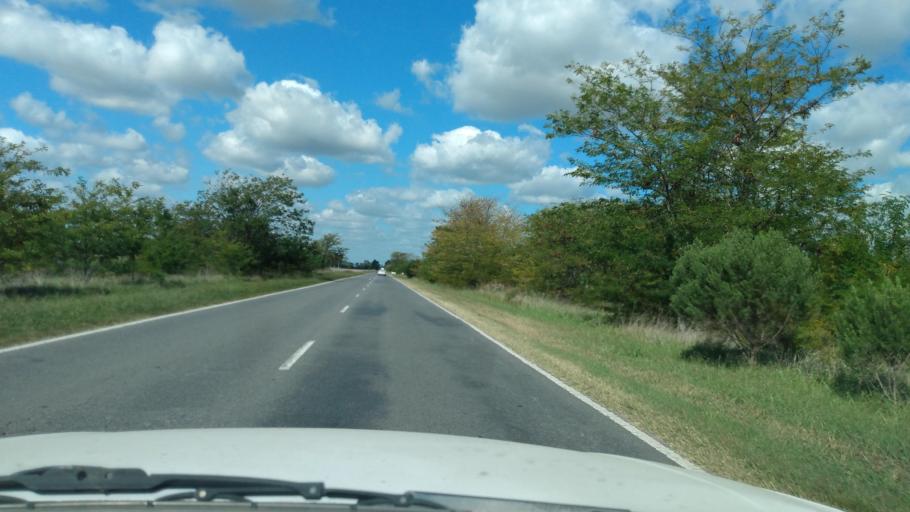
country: AR
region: Buenos Aires
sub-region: Partido de Navarro
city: Navarro
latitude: -34.9232
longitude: -59.3269
